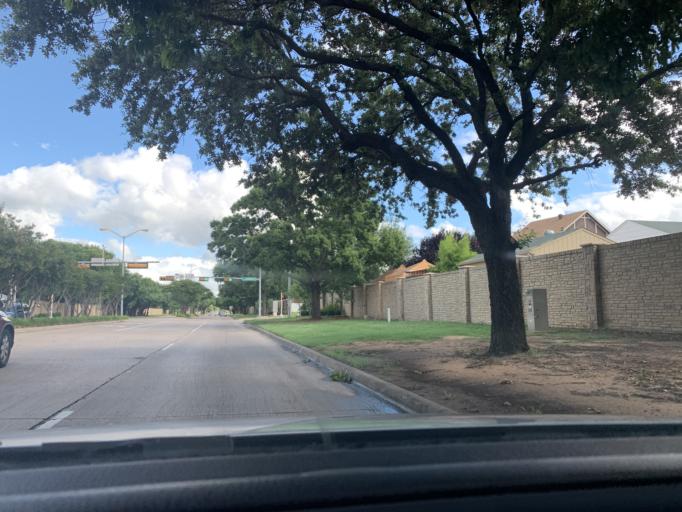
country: US
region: Texas
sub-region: Dallas County
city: Grand Prairie
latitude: 32.6686
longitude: -97.0441
